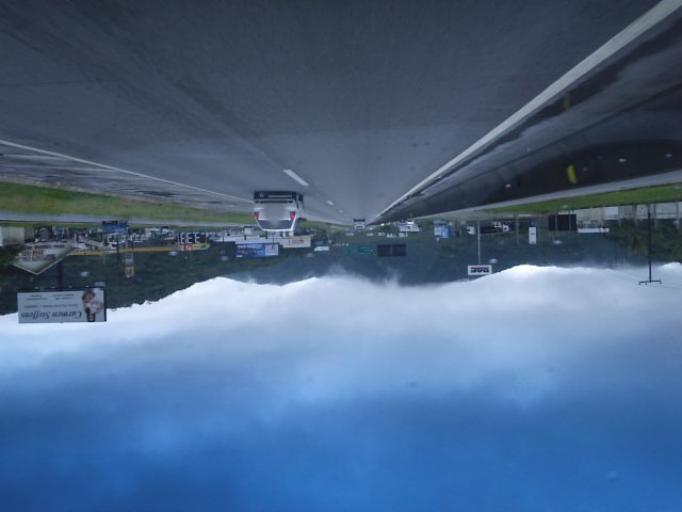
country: BR
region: Santa Catarina
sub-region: Itajai
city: Itajai
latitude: -26.9451
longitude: -48.6889
